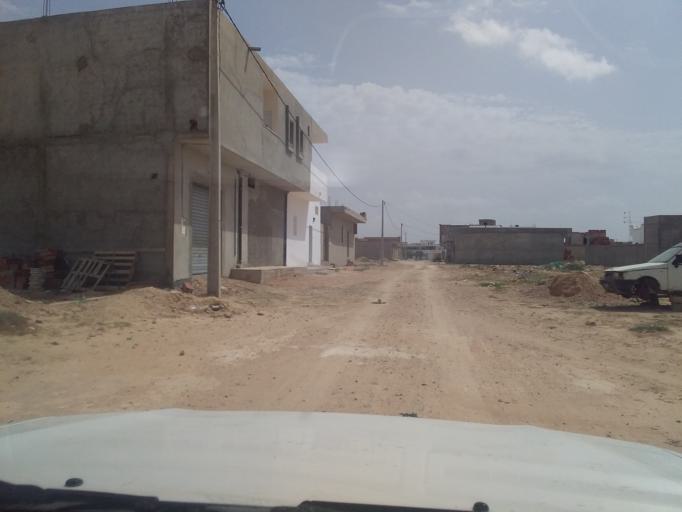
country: TN
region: Qabis
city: Matmata
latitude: 33.6215
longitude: 10.2711
